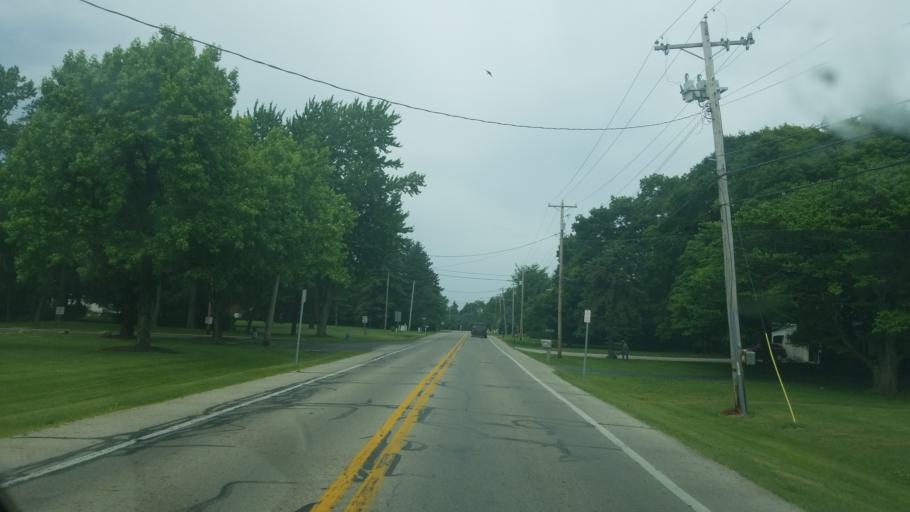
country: US
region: Ohio
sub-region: Franklin County
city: Worthington
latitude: 40.1003
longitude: -83.0104
